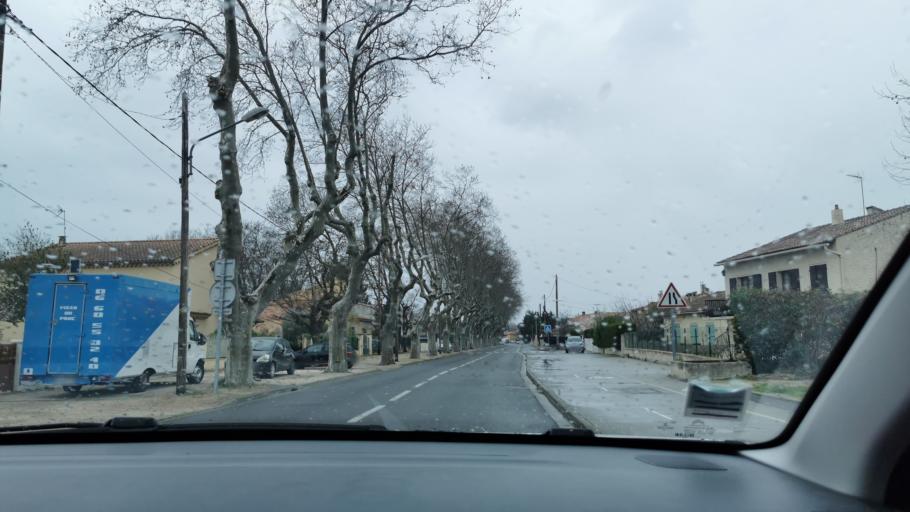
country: FR
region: Provence-Alpes-Cote d'Azur
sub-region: Departement des Bouches-du-Rhone
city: Pelissanne
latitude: 43.6300
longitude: 5.1613
